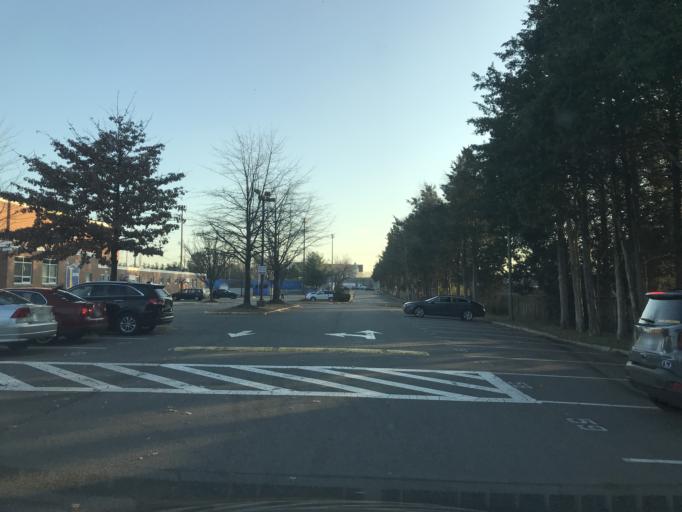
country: US
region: Virginia
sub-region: Fairfax County
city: Springfield
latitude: 38.7804
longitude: -77.1711
